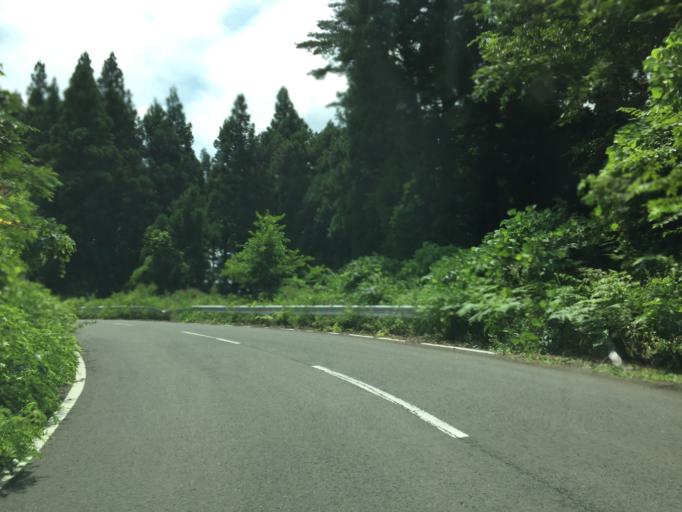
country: JP
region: Fukushima
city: Hobaramachi
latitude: 37.6501
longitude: 140.6494
